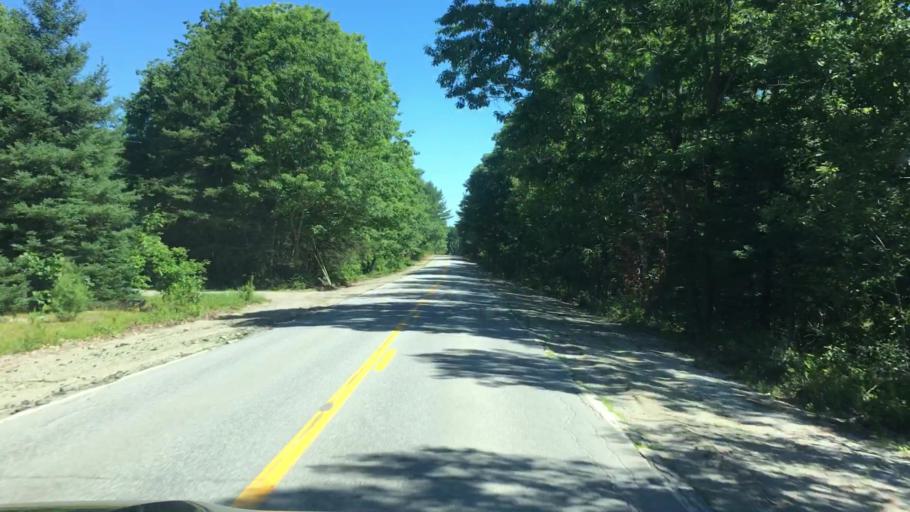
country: US
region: Maine
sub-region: Hancock County
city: Penobscot
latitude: 44.4416
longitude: -68.7061
